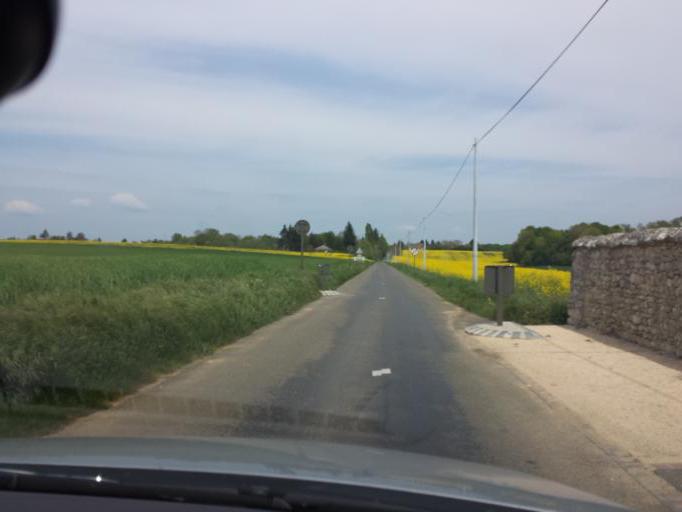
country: FR
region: Centre
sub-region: Departement d'Eure-et-Loir
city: Bu
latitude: 48.8460
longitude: 1.5477
